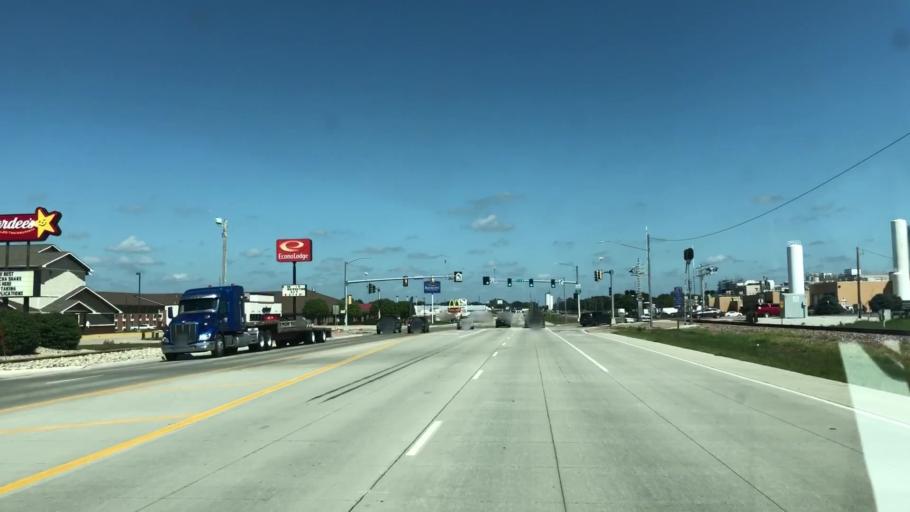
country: US
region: Iowa
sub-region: Plymouth County
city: Le Mars
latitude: 42.7781
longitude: -96.1865
